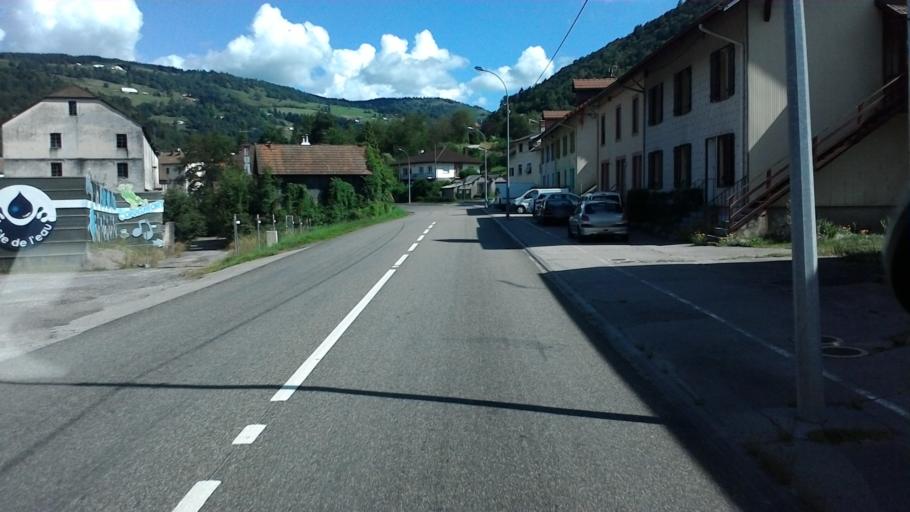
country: FR
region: Lorraine
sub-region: Departement des Vosges
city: Cornimont
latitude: 47.9687
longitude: 6.8335
